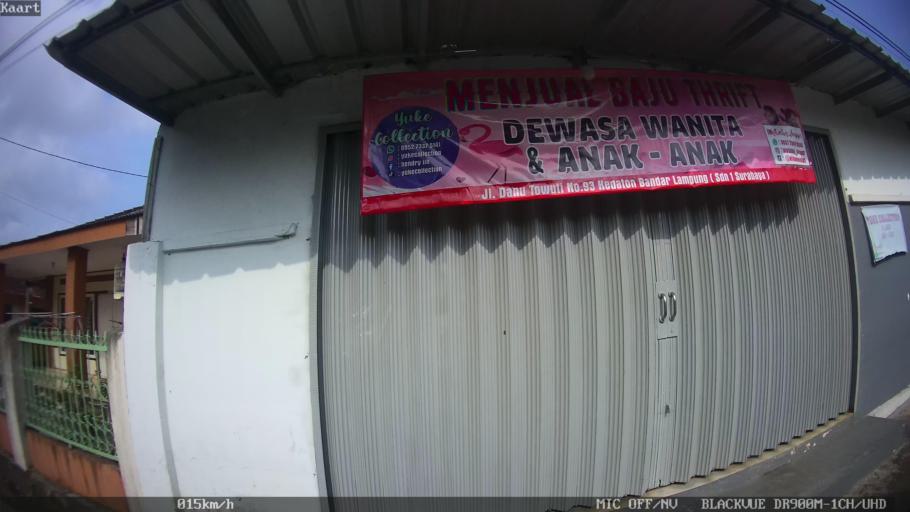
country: ID
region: Lampung
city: Kedaton
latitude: -5.3882
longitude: 105.2652
